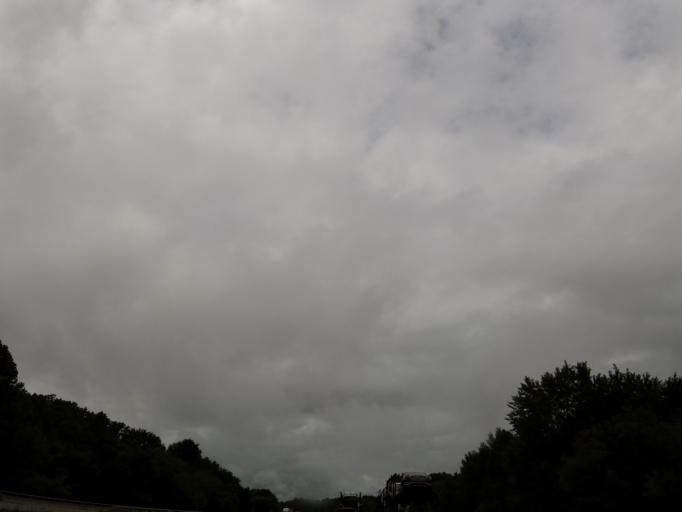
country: US
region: Illinois
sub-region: Jefferson County
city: Mount Vernon
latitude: 38.3607
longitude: -89.0125
